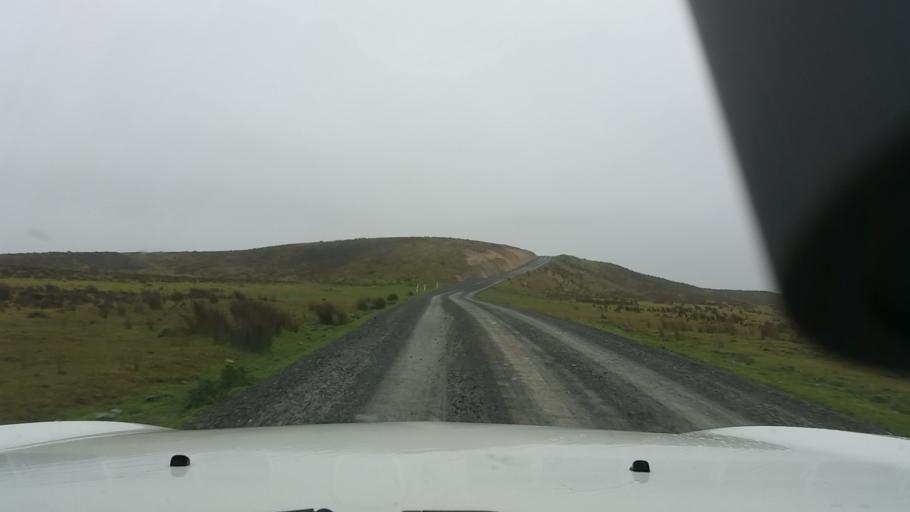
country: NZ
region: Chatham Islands
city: Waitangi
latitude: -43.8003
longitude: -176.6918
